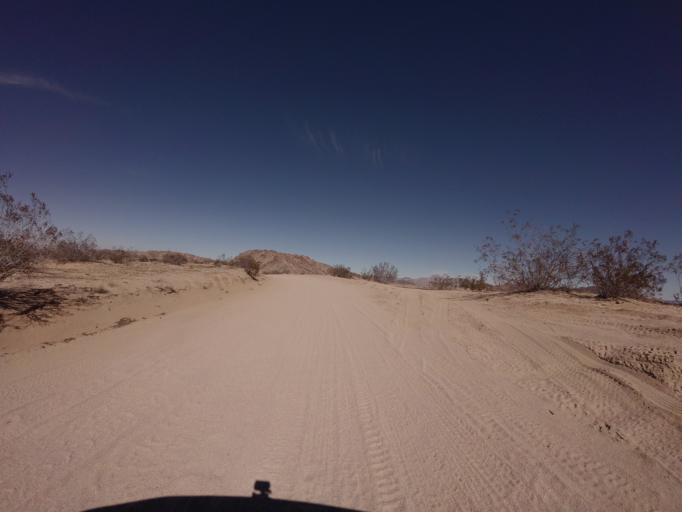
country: US
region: California
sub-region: San Bernardino County
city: Joshua Tree
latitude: 34.3043
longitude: -116.3965
